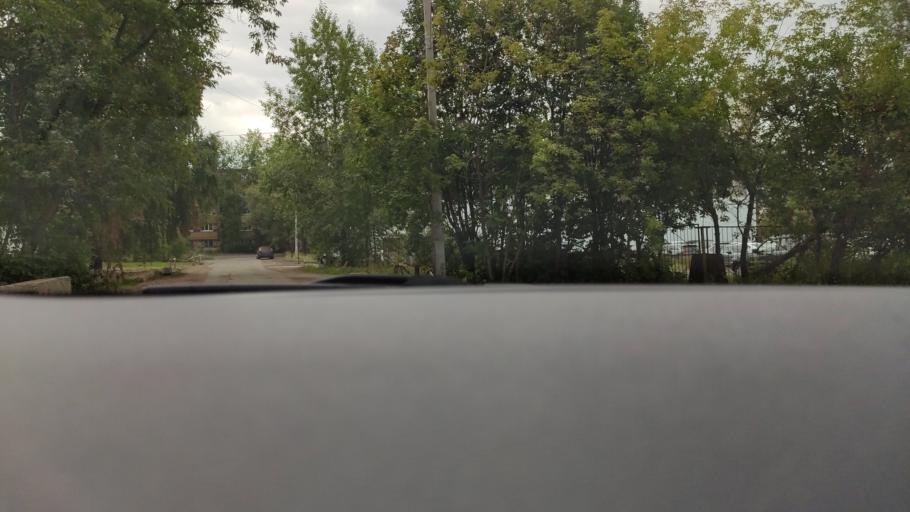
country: RU
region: Perm
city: Perm
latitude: 58.0652
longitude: 56.3528
